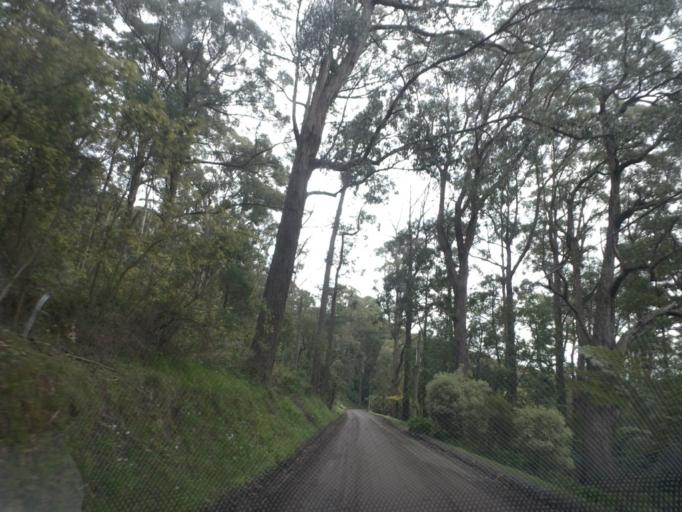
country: AU
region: Victoria
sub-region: Yarra Ranges
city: Olinda
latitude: -37.8524
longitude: 145.3586
